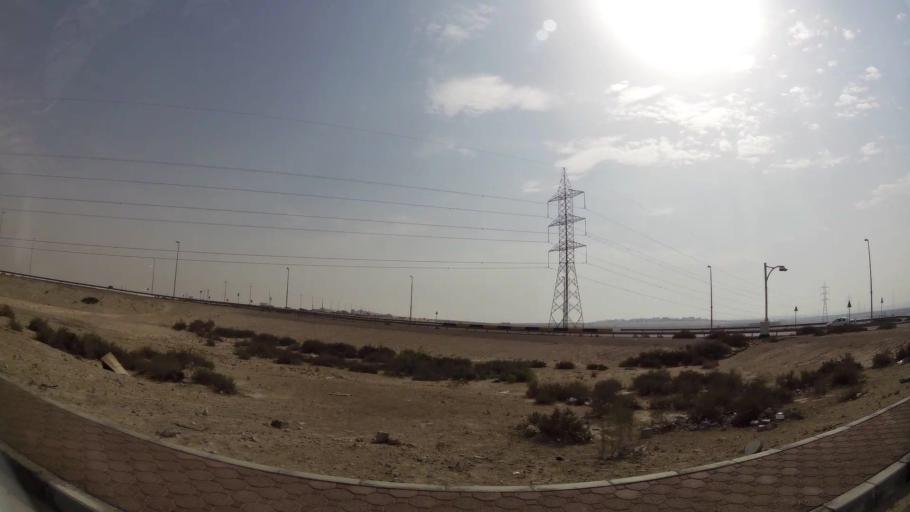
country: AE
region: Abu Dhabi
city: Abu Dhabi
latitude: 24.2760
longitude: 54.6764
